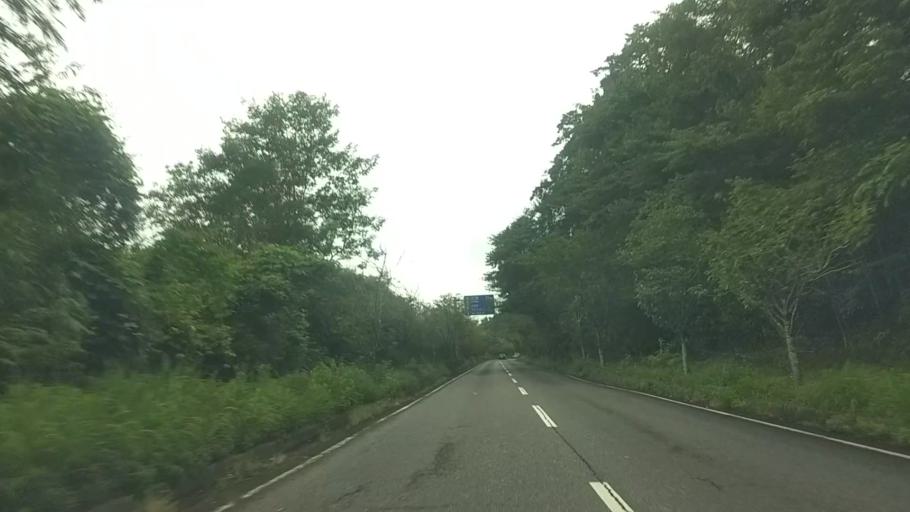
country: JP
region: Chiba
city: Kisarazu
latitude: 35.3839
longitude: 140.0064
